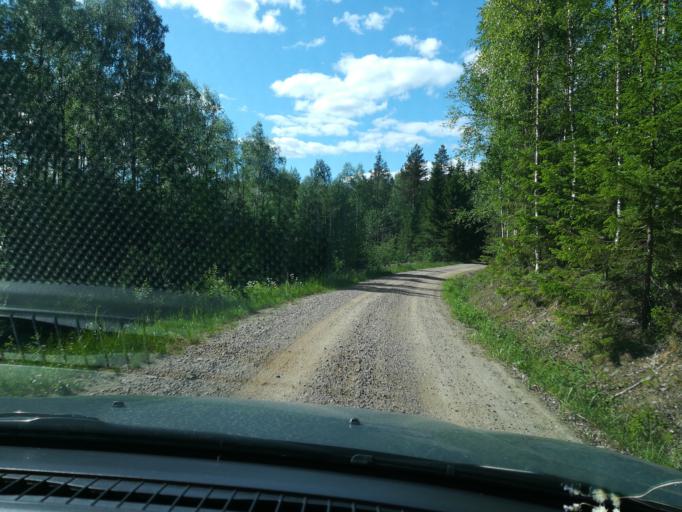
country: FI
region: Southern Savonia
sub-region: Mikkeli
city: Puumala
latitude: 61.6575
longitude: 28.1622
